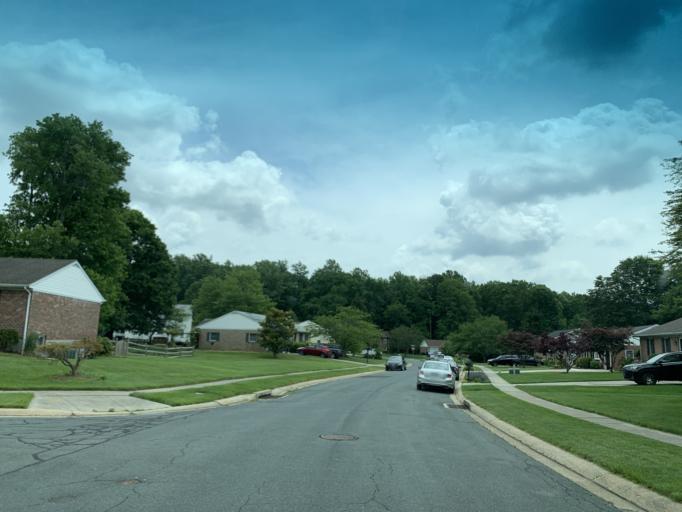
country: US
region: Maryland
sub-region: Harford County
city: Bel Air South
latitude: 39.5386
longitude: -76.2952
